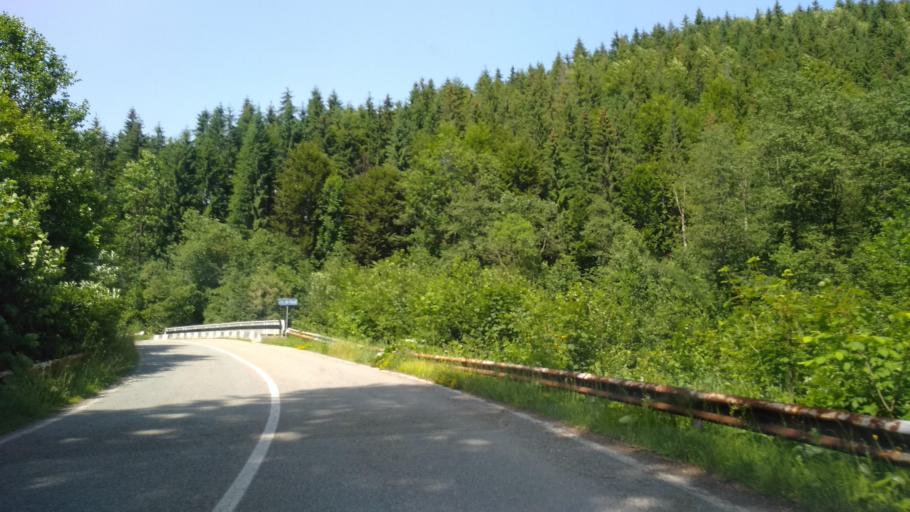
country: RO
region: Hunedoara
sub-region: Comuna Uricani
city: Uricani
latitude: 45.2847
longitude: 22.9705
